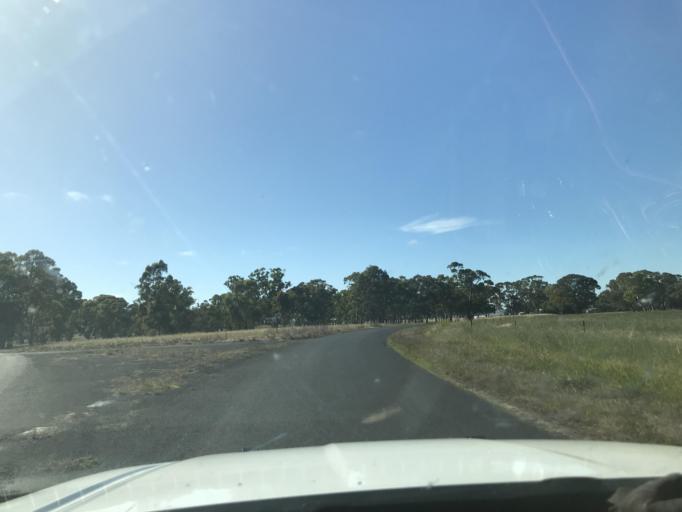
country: AU
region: Victoria
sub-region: Horsham
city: Horsham
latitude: -37.0415
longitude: 141.7435
